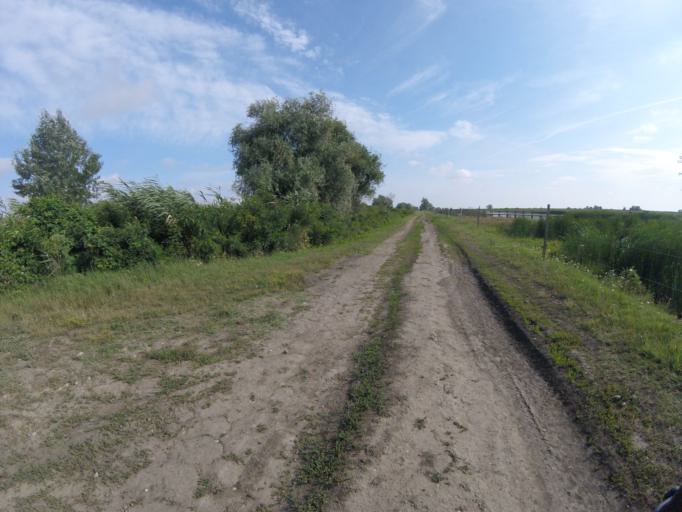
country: HU
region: Hajdu-Bihar
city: Hortobagy
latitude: 47.6129
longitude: 21.0732
